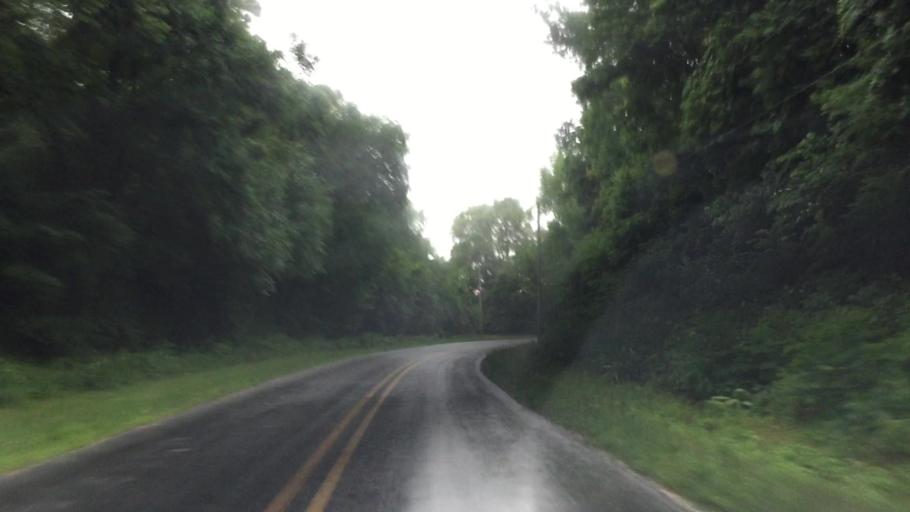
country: US
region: Iowa
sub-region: Lee County
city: Fort Madison
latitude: 40.6108
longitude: -91.2814
